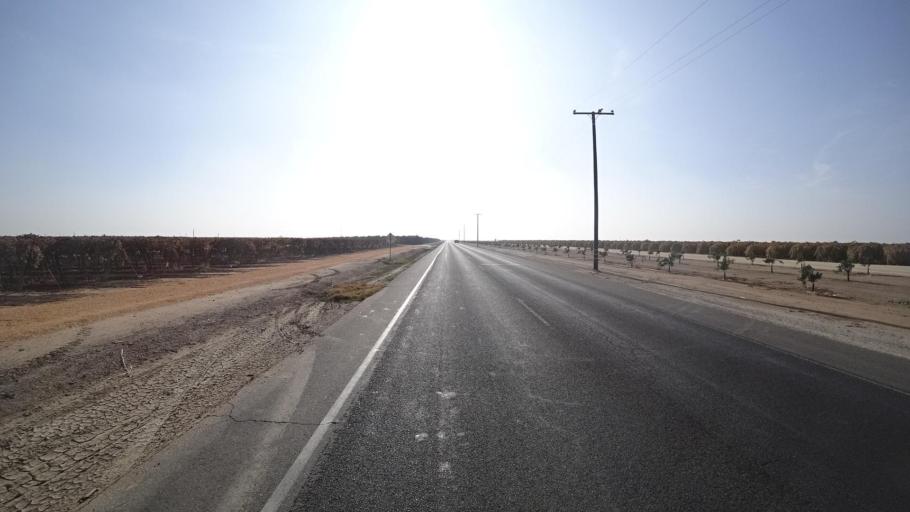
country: US
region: California
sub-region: Tulare County
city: Richgrove
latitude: 35.7315
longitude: -119.1513
